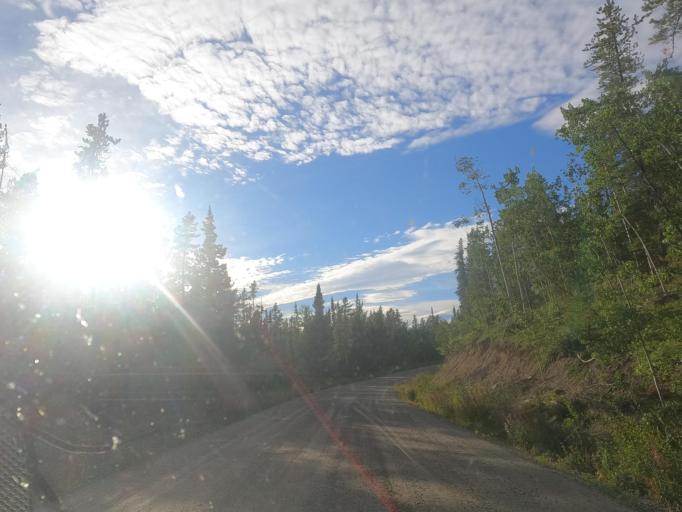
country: CA
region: Yukon
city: Whitehorse
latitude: 60.7548
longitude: -135.0357
